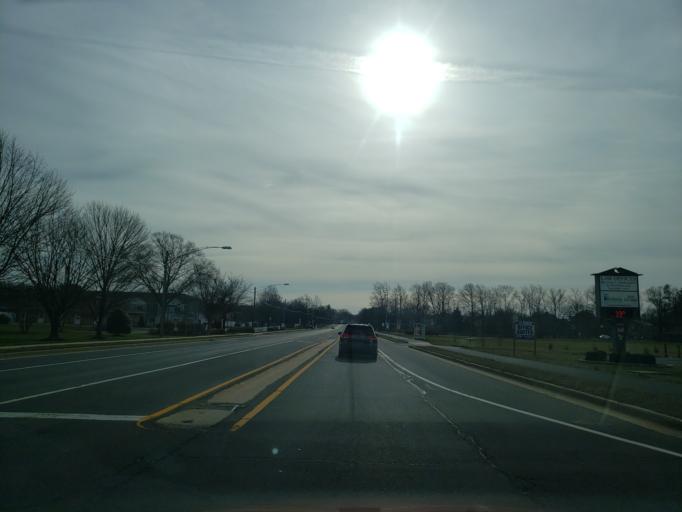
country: US
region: Delaware
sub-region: Kent County
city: Dover
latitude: 39.1761
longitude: -75.5536
